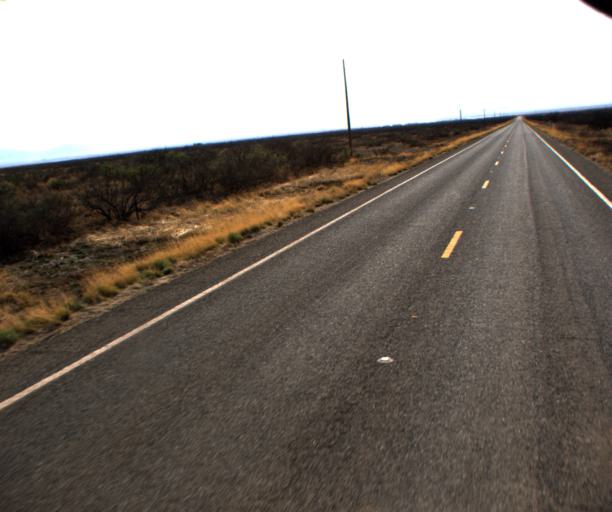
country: US
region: Arizona
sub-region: Cochise County
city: Willcox
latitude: 32.1953
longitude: -109.7244
